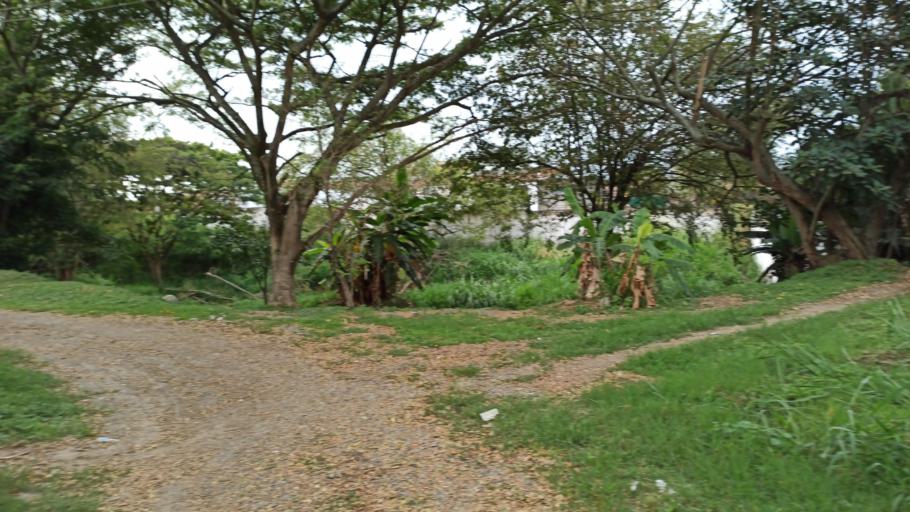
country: CO
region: Valle del Cauca
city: Palmira
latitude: 3.5307
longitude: -76.2835
